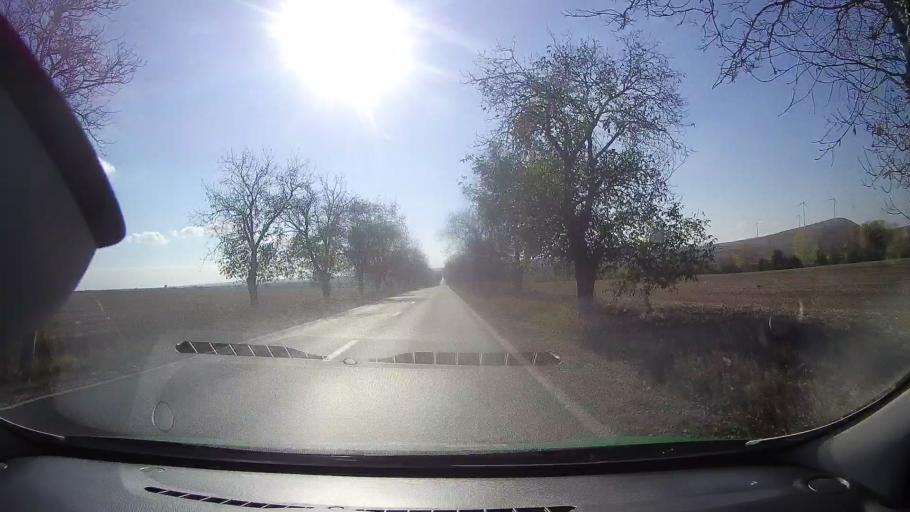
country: RO
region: Tulcea
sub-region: Comuna Ceamurlia de Jos
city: Ceamurlia de Jos
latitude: 44.7793
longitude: 28.6890
